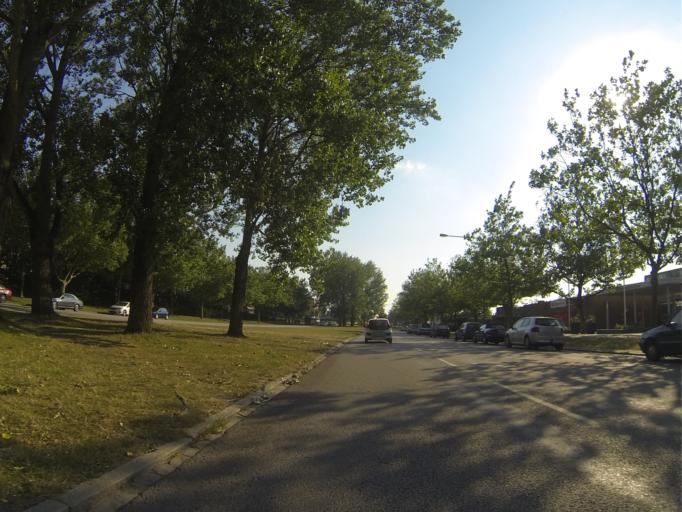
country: SE
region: Skane
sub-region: Malmo
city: Malmoe
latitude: 55.5812
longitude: 12.9776
